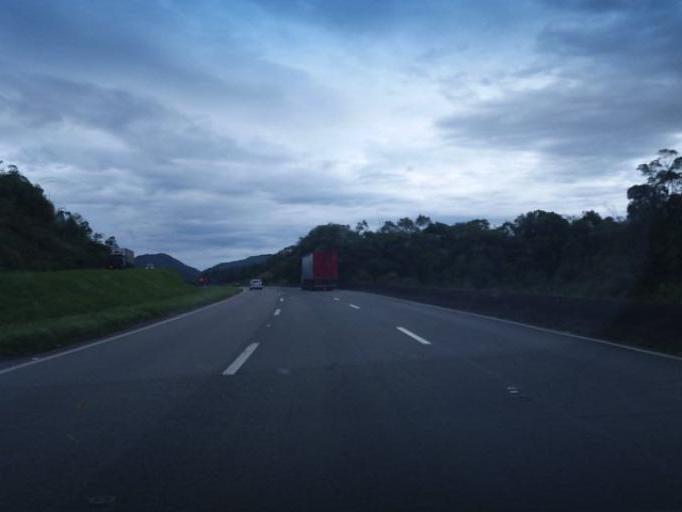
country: BR
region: Sao Paulo
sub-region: Cajati
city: Cajati
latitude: -24.9995
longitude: -48.5091
